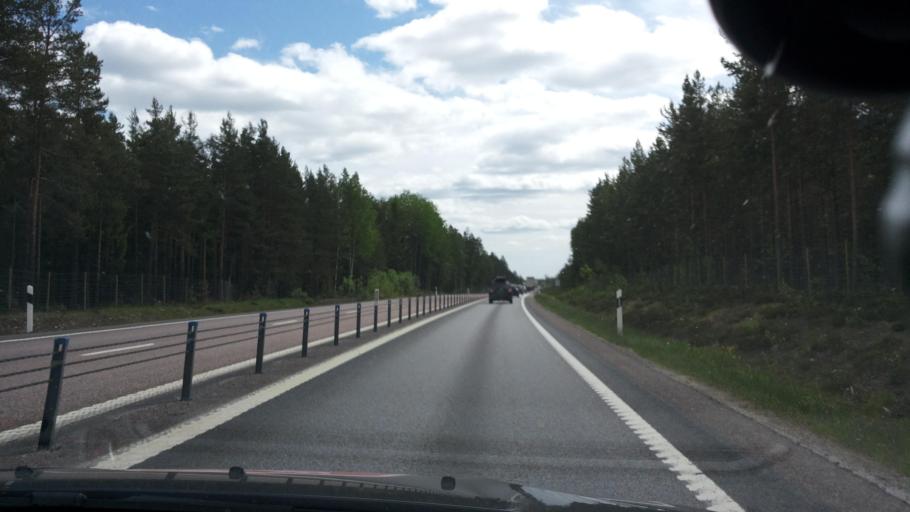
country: SE
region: Gaevleborg
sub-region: Gavle Kommun
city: Norrsundet
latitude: 60.9881
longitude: 17.0088
